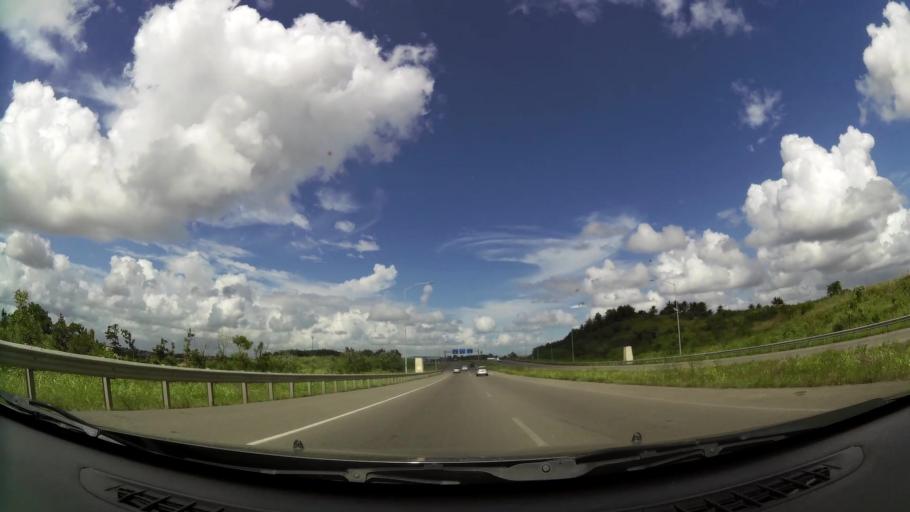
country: TT
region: City of San Fernando
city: Mon Repos
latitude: 10.2480
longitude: -61.4430
